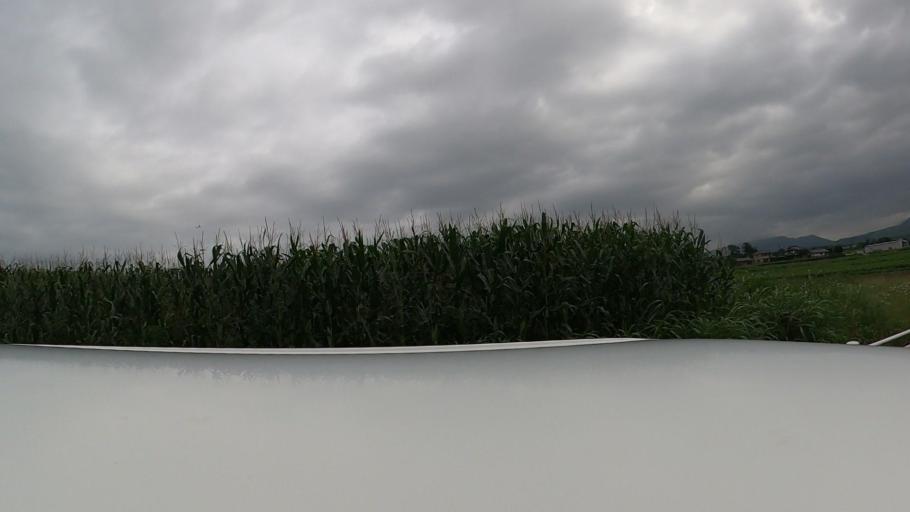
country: JP
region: Kumamoto
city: Ozu
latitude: 32.8380
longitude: 130.9001
